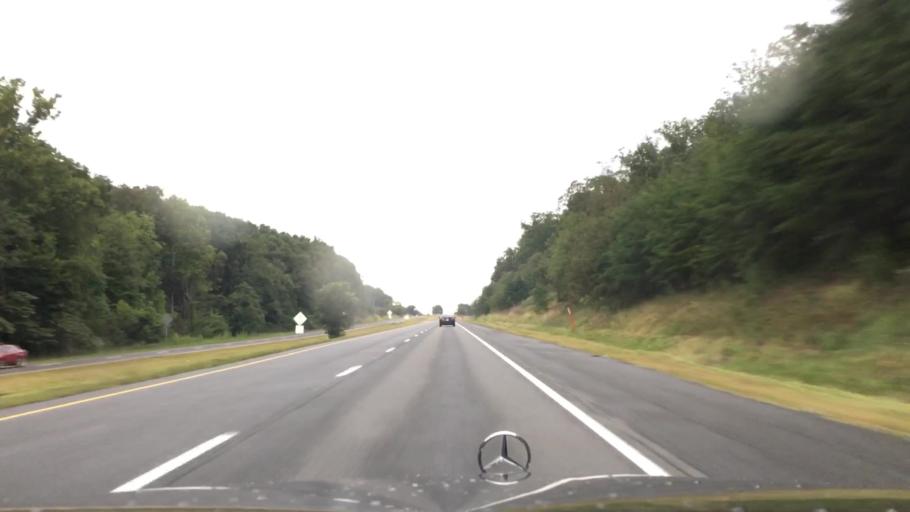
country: US
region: Virginia
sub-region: Frederick County
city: Shawnee Land
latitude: 39.3482
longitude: -78.3089
